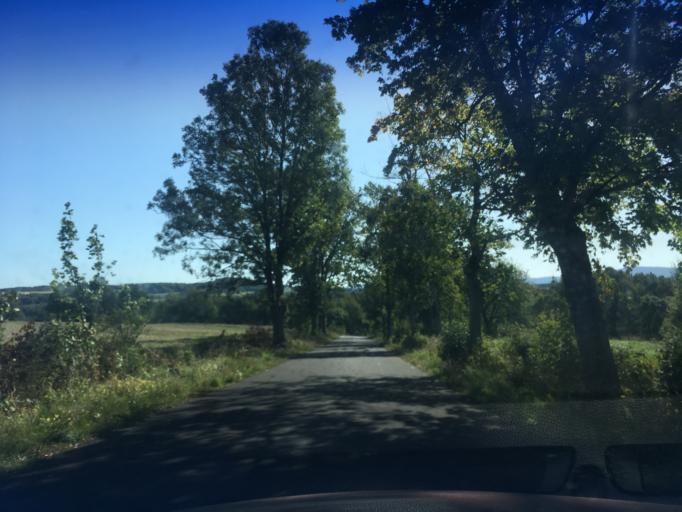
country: PL
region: Lower Silesian Voivodeship
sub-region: Powiat lubanski
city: Lesna
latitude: 51.0216
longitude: 15.1938
